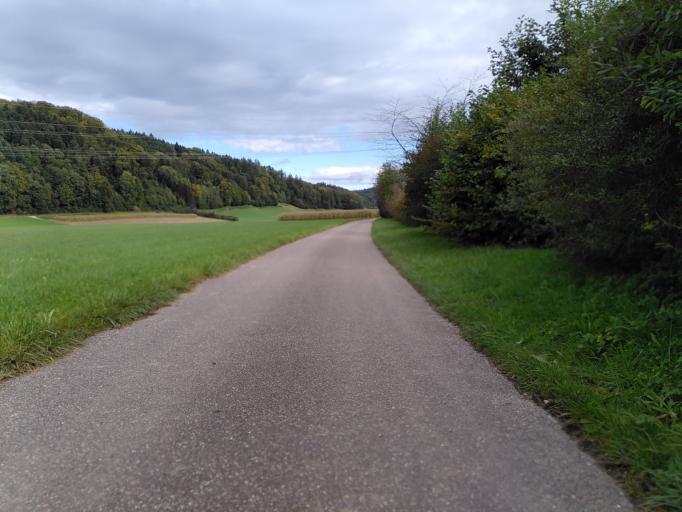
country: CH
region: Bern
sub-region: Emmental District
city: Wynigen
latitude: 47.1128
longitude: 7.6669
